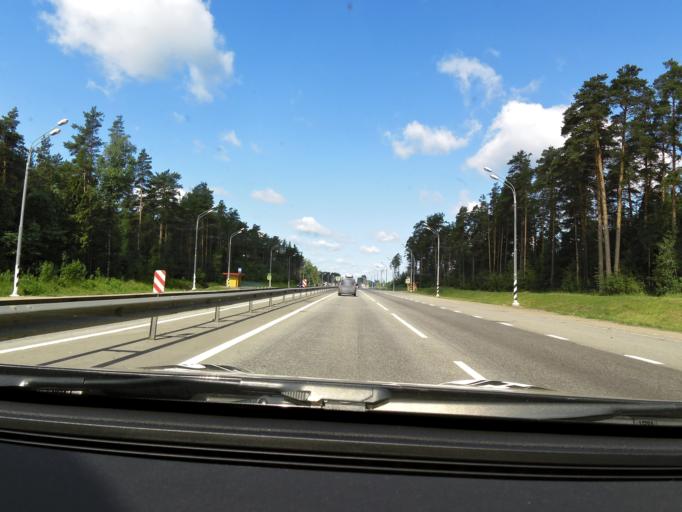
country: RU
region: Tverskaya
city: Tver
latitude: 56.9042
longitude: 35.6556
